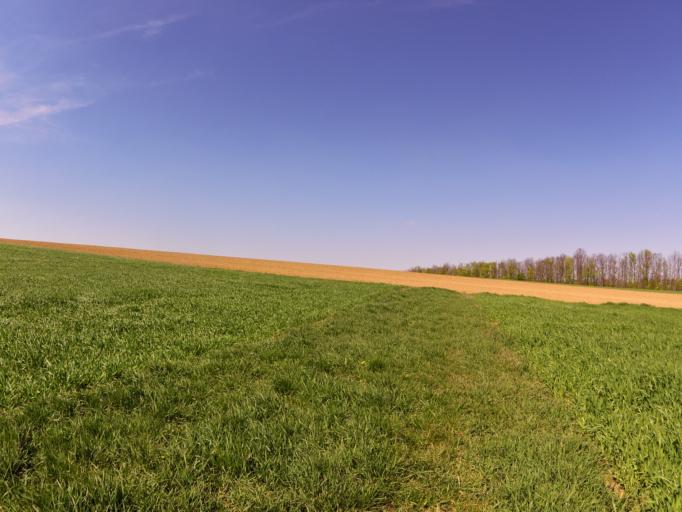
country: DE
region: Bavaria
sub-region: Regierungsbezirk Unterfranken
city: Rottendorf
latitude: 49.7931
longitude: 10.0559
